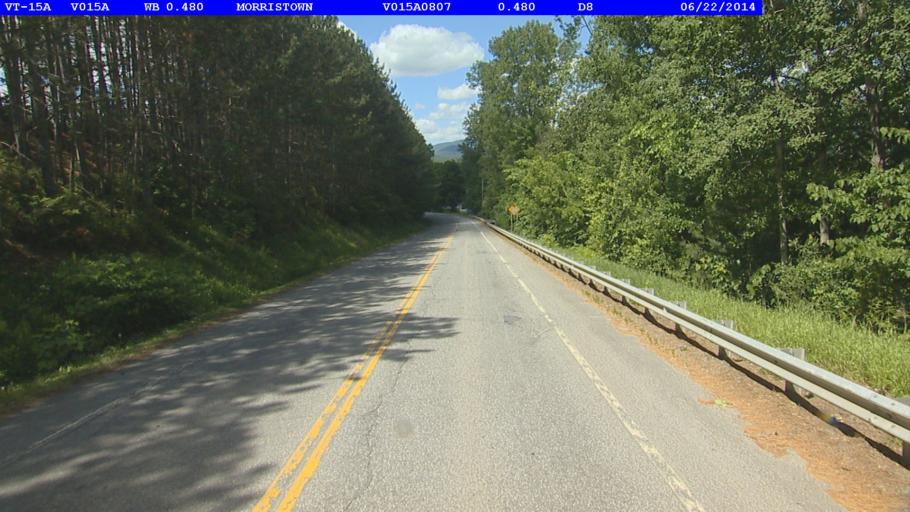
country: US
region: Vermont
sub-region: Lamoille County
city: Morrisville
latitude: 44.5641
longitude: -72.5895
